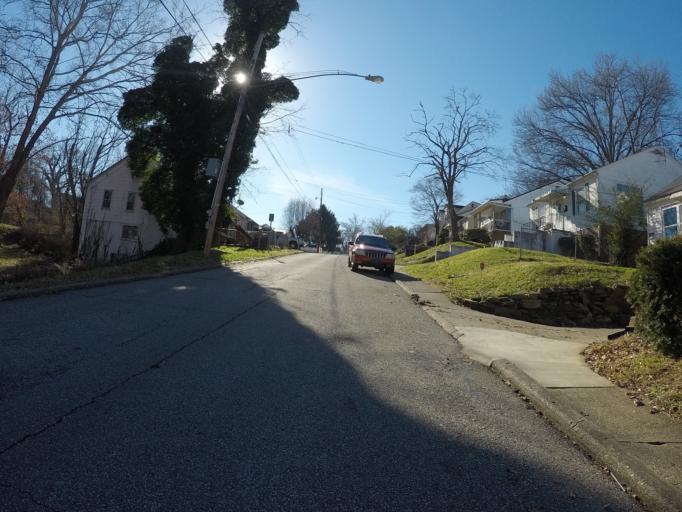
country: US
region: West Virginia
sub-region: Cabell County
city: Huntington
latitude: 38.4082
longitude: -82.4008
